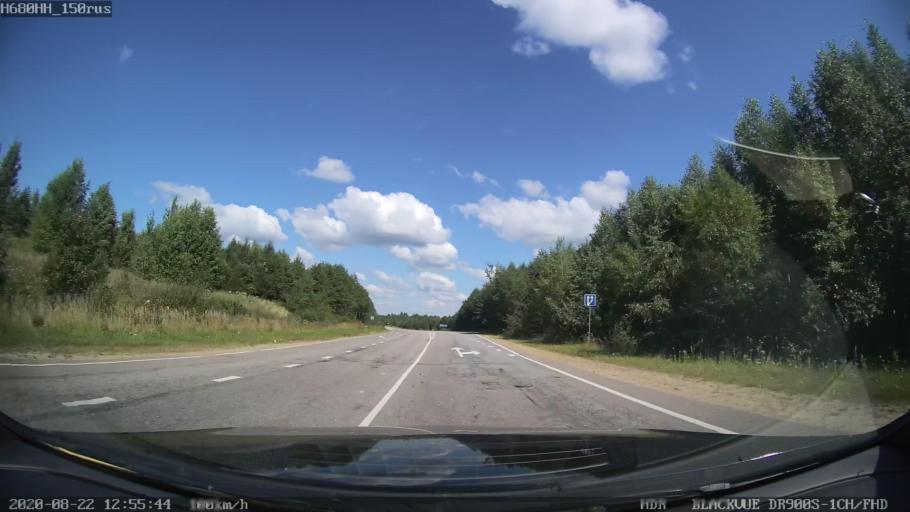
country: RU
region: Tverskaya
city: Rameshki
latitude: 57.5465
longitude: 36.3077
